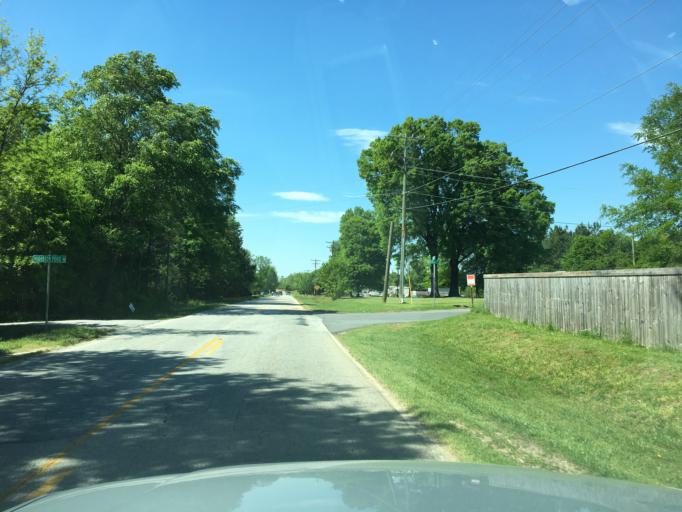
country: US
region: South Carolina
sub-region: Spartanburg County
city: Fairforest
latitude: 34.9814
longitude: -82.0318
